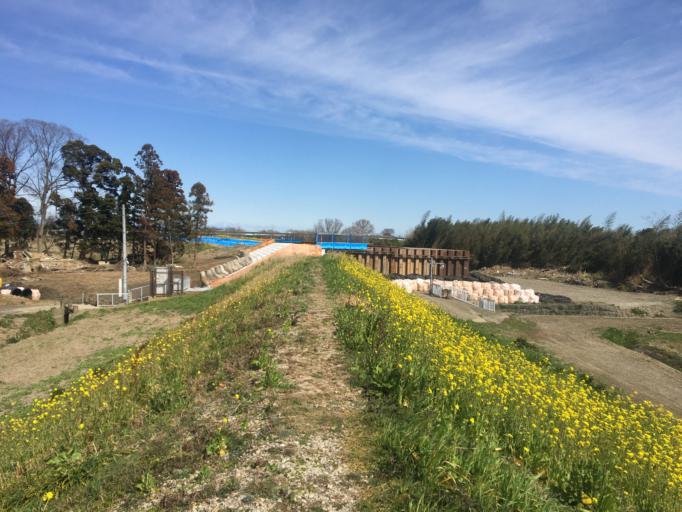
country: JP
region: Saitama
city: Sakado
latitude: 35.9977
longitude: 139.4223
